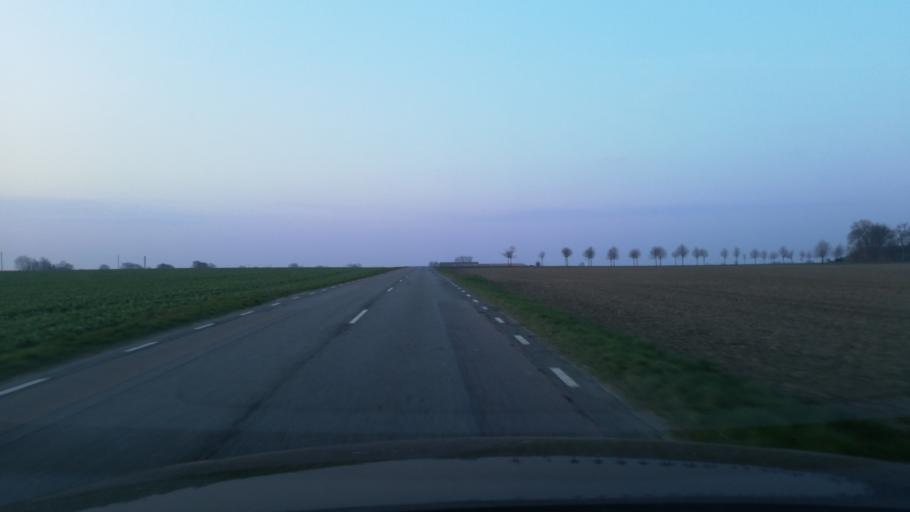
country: SE
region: Skane
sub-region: Tomelilla Kommun
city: Tomelilla
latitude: 55.4688
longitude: 14.0976
